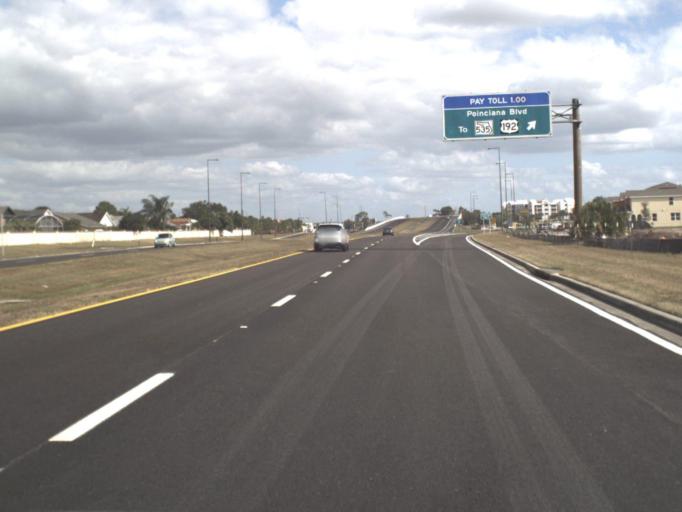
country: US
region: Florida
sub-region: Osceola County
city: Celebration
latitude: 28.3400
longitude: -81.4910
